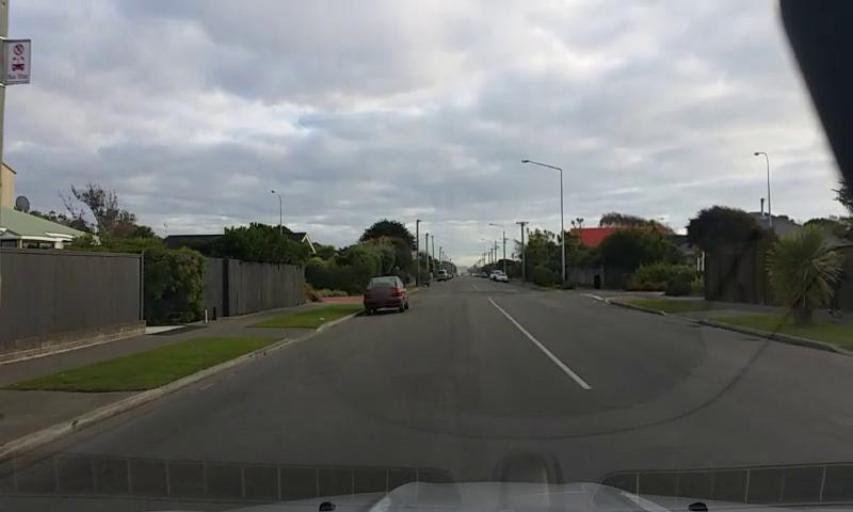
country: NZ
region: Canterbury
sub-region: Christchurch City
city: Christchurch
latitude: -43.5326
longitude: 172.7367
